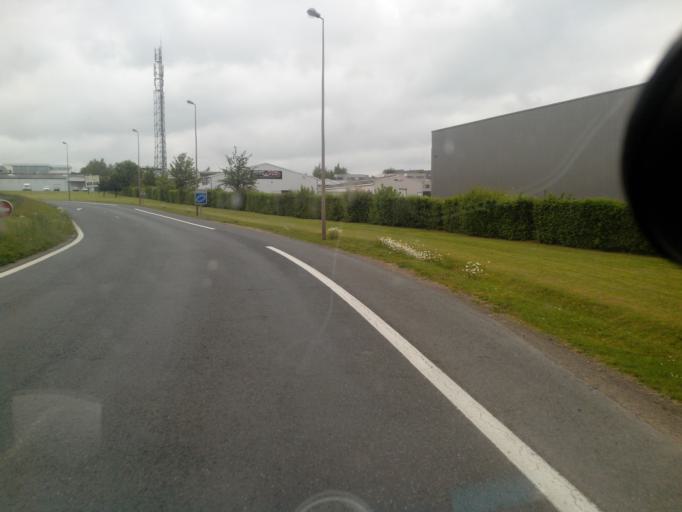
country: FR
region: Lower Normandy
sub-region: Departement du Calvados
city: Bretteville-sur-Odon
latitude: 49.1643
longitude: -0.4256
